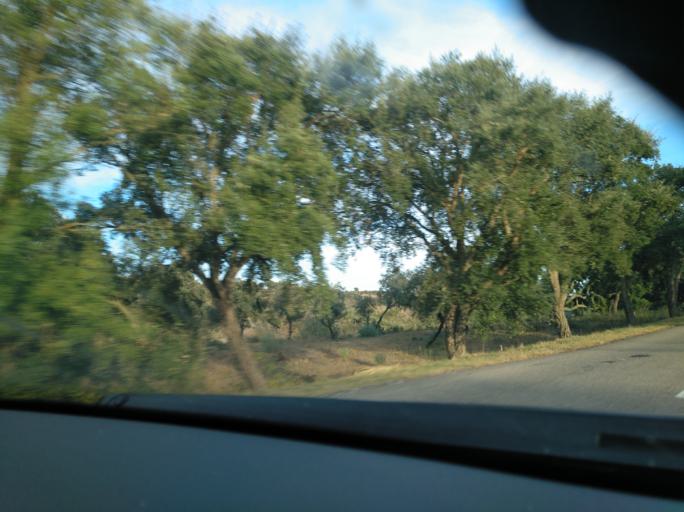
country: PT
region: Portalegre
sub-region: Avis
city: Avis
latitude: 38.8721
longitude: -7.8249
